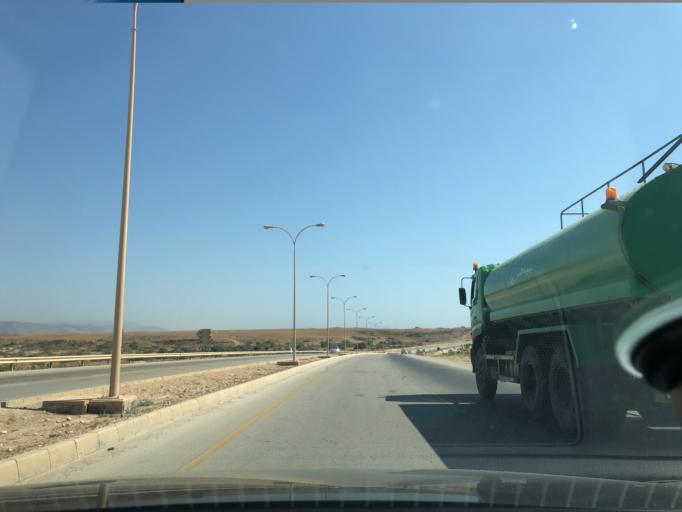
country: OM
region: Zufar
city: Salalah
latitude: 17.0505
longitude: 54.3271
